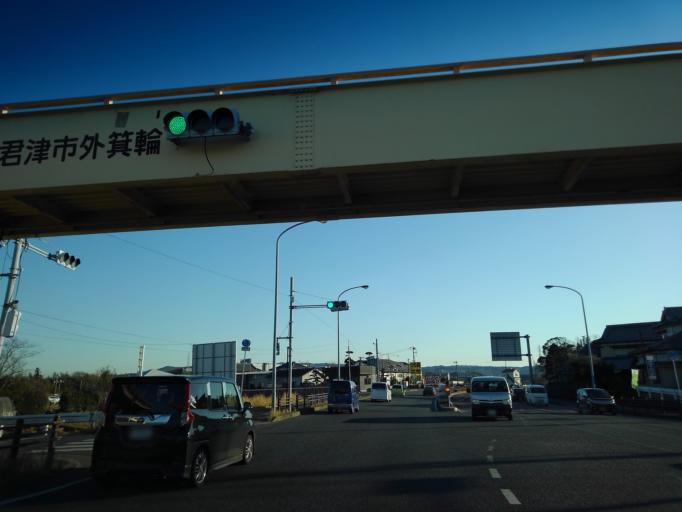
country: JP
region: Chiba
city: Kimitsu
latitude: 35.3165
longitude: 139.9270
